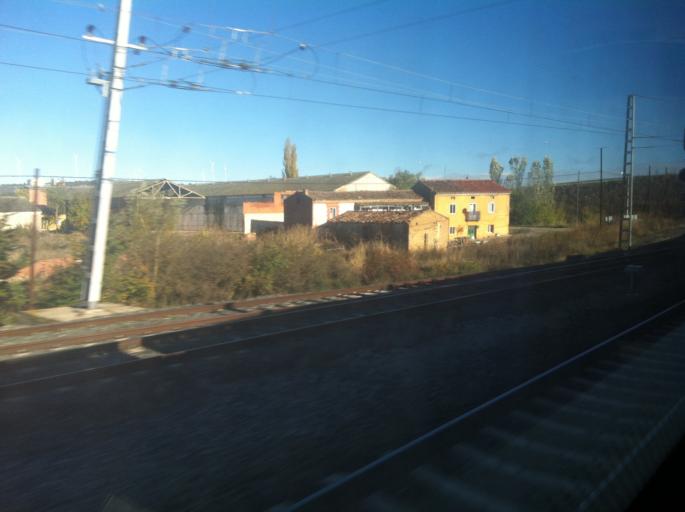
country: ES
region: Castille and Leon
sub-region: Provincia de Burgos
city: Villaquiran de los Infantes
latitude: 42.2164
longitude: -3.9991
